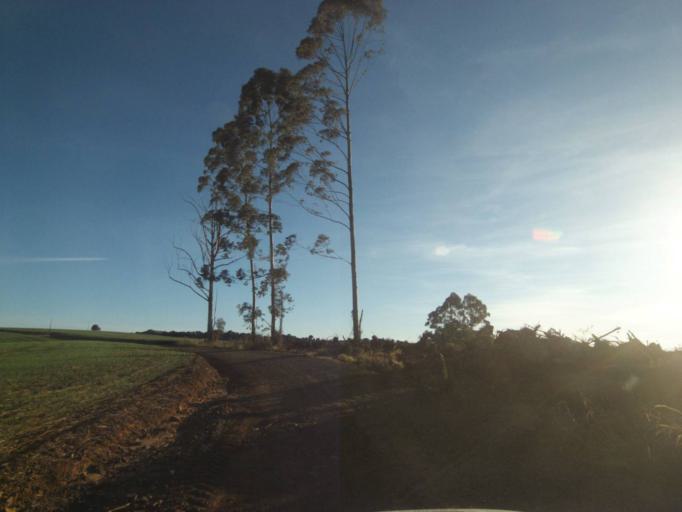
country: BR
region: Parana
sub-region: Telemaco Borba
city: Telemaco Borba
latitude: -24.4805
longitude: -50.5925
